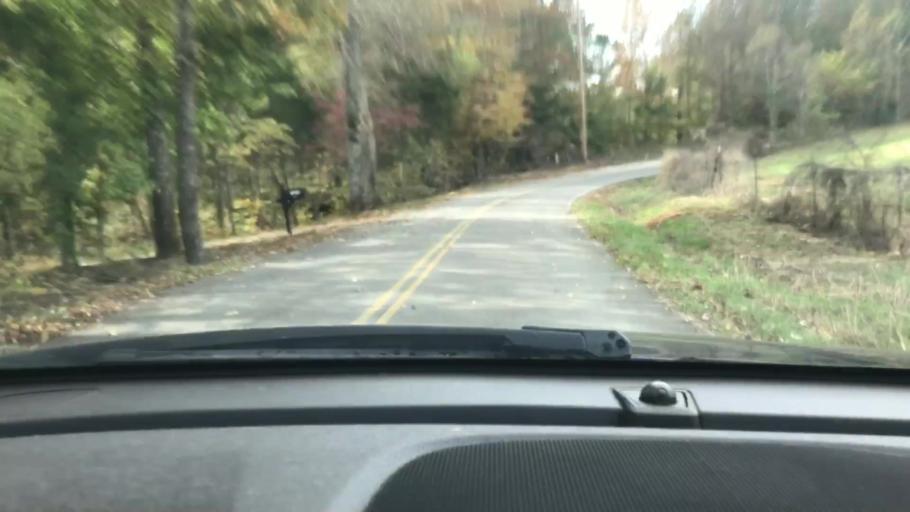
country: US
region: Tennessee
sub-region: Dickson County
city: Charlotte
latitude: 36.1937
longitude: -87.2925
